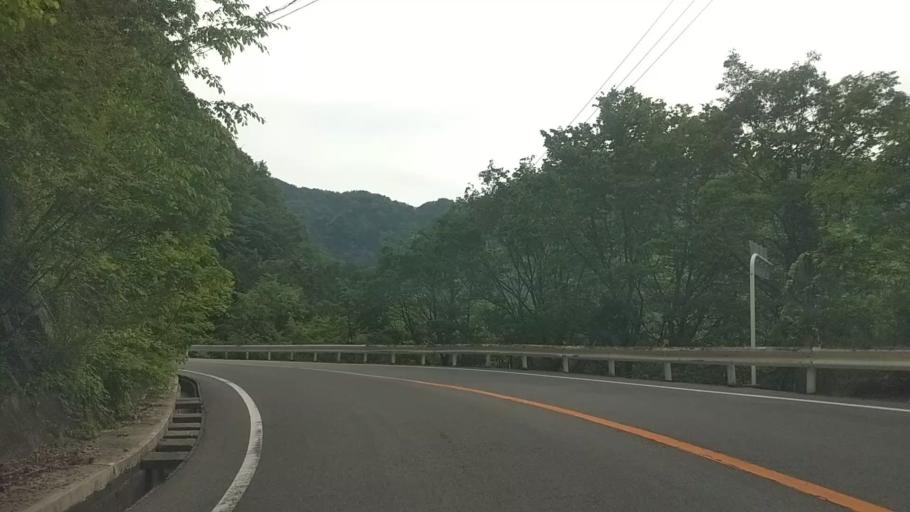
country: JP
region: Yamanashi
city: Fujikawaguchiko
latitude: 35.5175
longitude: 138.6186
